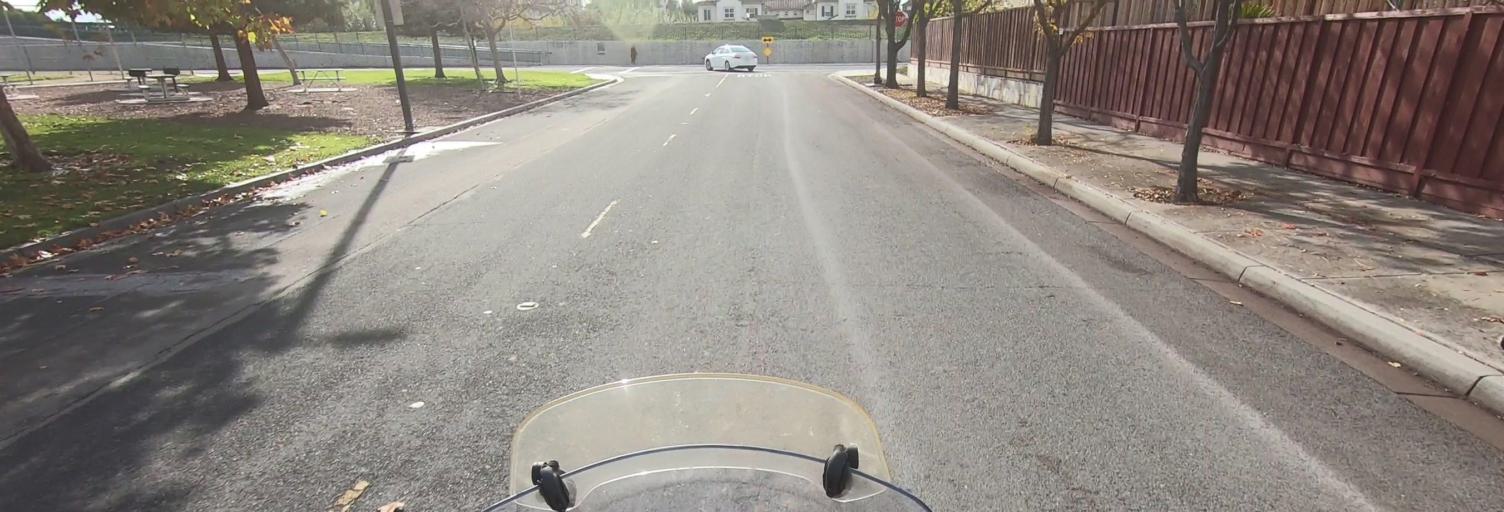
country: US
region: California
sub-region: Santa Clara County
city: Milpitas
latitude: 37.4377
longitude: -121.8965
